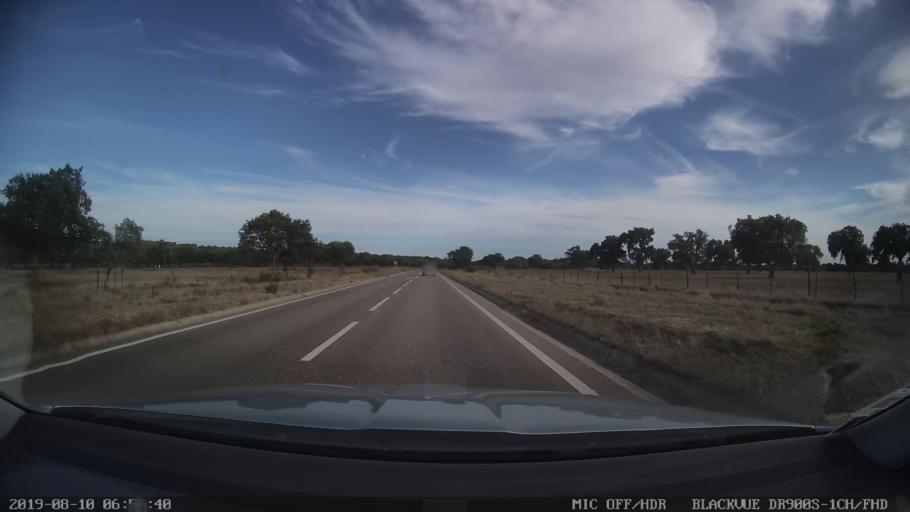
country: PT
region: Santarem
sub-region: Benavente
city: Poceirao
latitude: 38.8907
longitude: -8.7468
